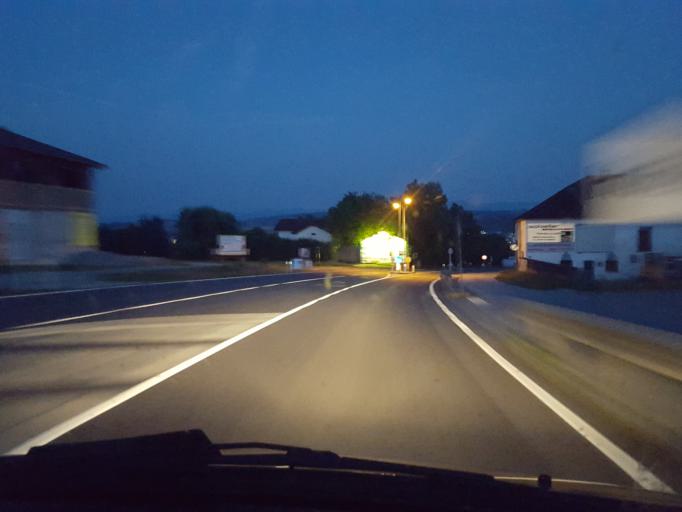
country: AT
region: Lower Austria
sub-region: Politischer Bezirk Scheibbs
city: Wieselburg
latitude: 48.1438
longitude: 15.1339
